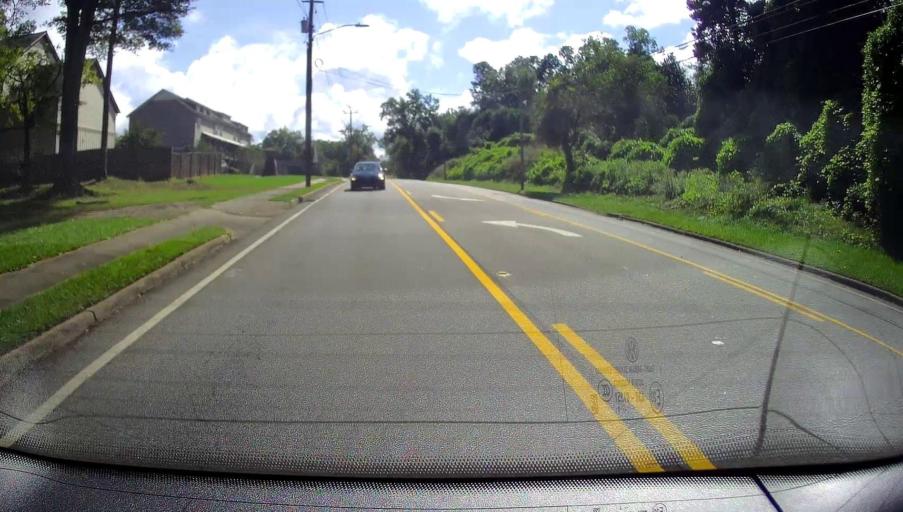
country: US
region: Georgia
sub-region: Baldwin County
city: Milledgeville
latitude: 33.0882
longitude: -83.2360
